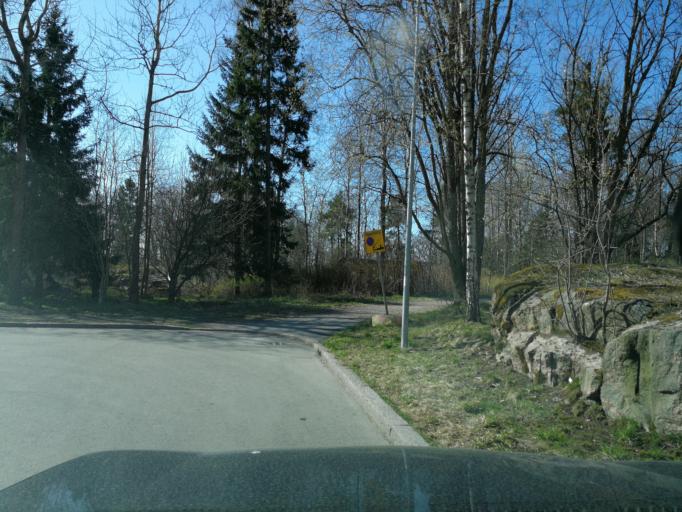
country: FI
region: Uusimaa
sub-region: Helsinki
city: Helsinki
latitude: 60.1477
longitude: 24.8877
